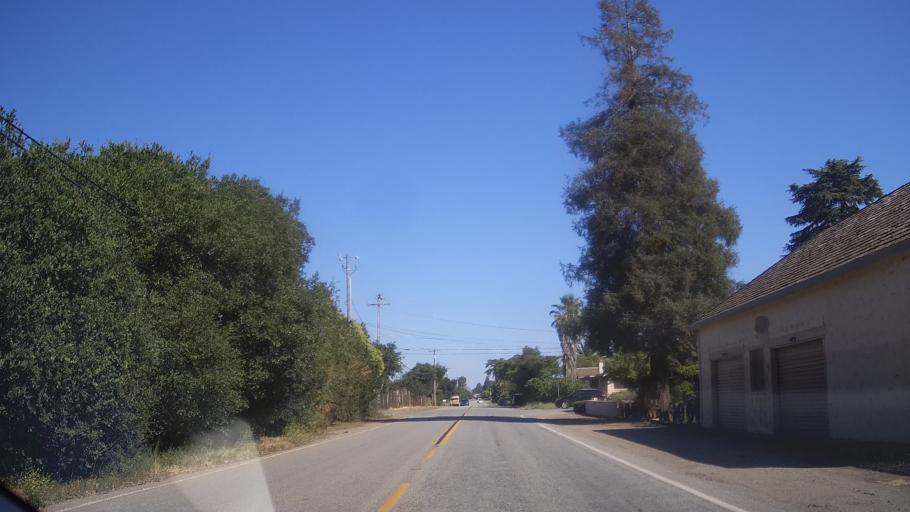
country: US
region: California
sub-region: Santa Clara County
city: Morgan Hill
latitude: 37.1610
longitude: -121.6872
